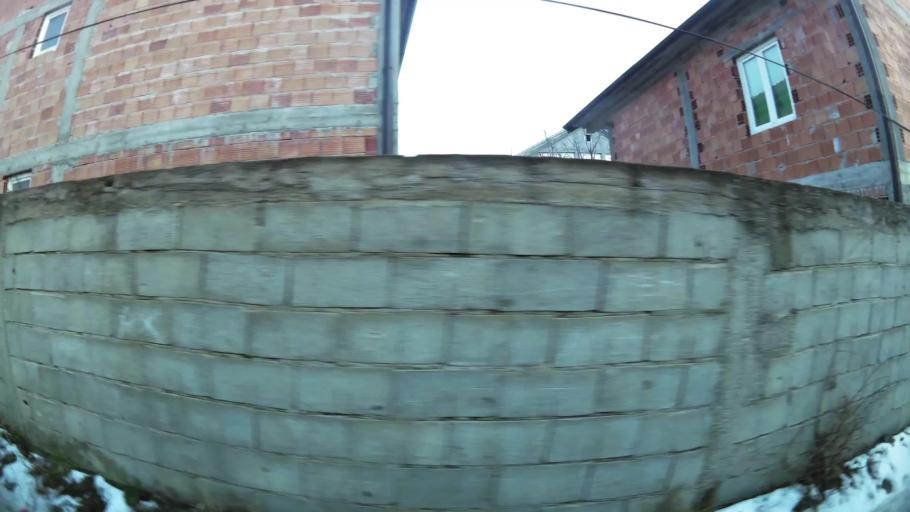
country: MK
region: Aracinovo
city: Arachinovo
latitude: 42.0243
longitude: 21.5609
